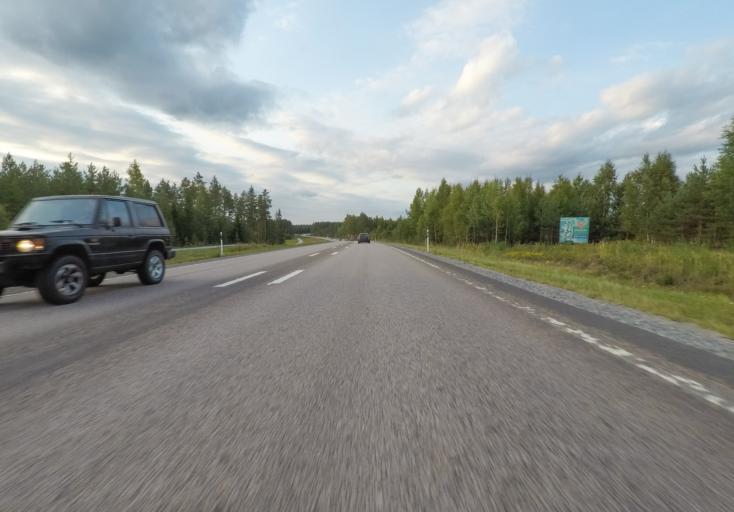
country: FI
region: Paijanne Tavastia
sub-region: Lahti
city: Hartola
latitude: 61.5510
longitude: 26.0086
